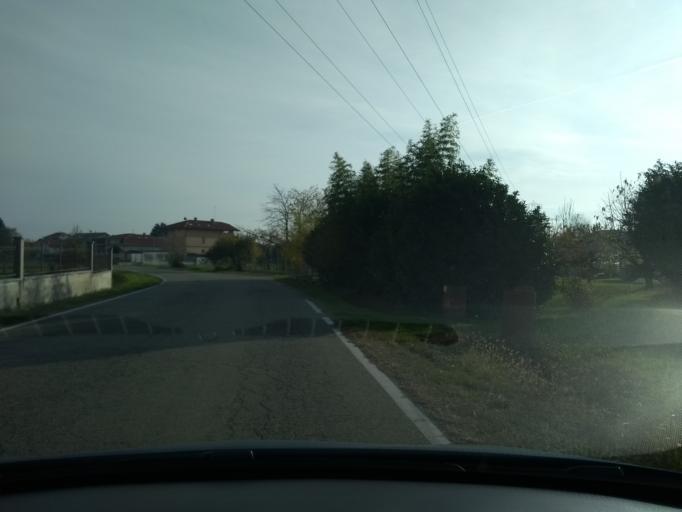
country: IT
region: Piedmont
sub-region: Provincia di Torino
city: Mathi
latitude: 45.2638
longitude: 7.5337
